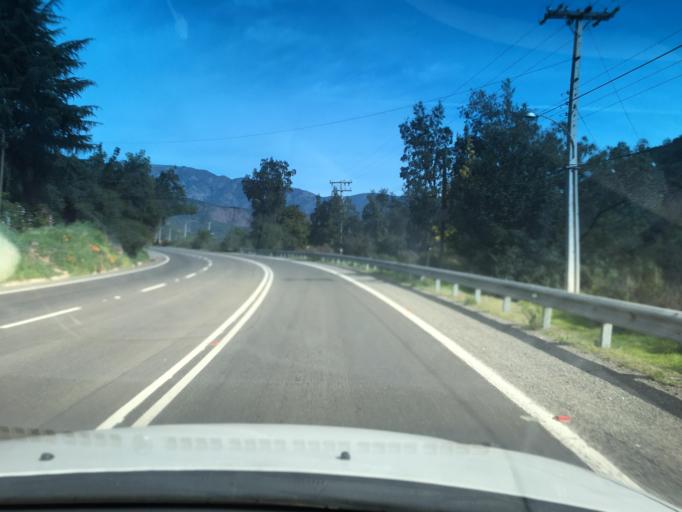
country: CL
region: Valparaiso
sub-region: Provincia de Marga Marga
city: Limache
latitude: -33.0569
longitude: -71.0408
